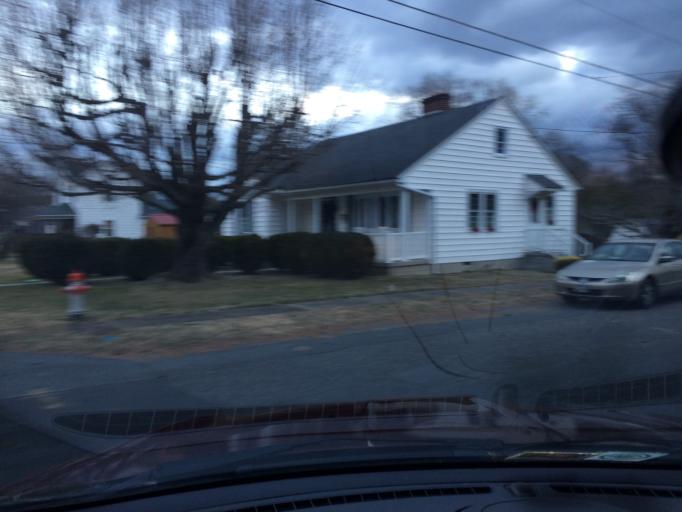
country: US
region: Virginia
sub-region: Alleghany County
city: Clifton Forge
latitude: 37.8224
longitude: -79.8187
